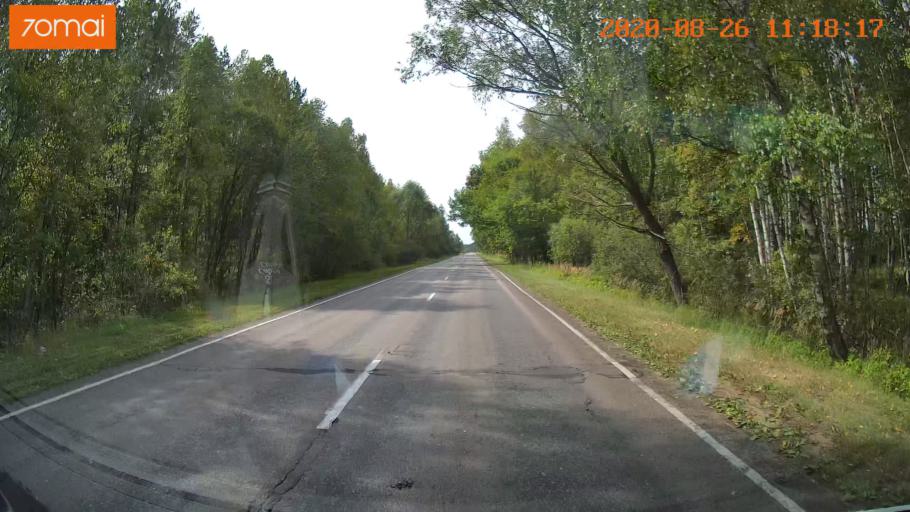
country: RU
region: Rjazan
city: Shilovo
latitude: 54.4114
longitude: 41.0997
